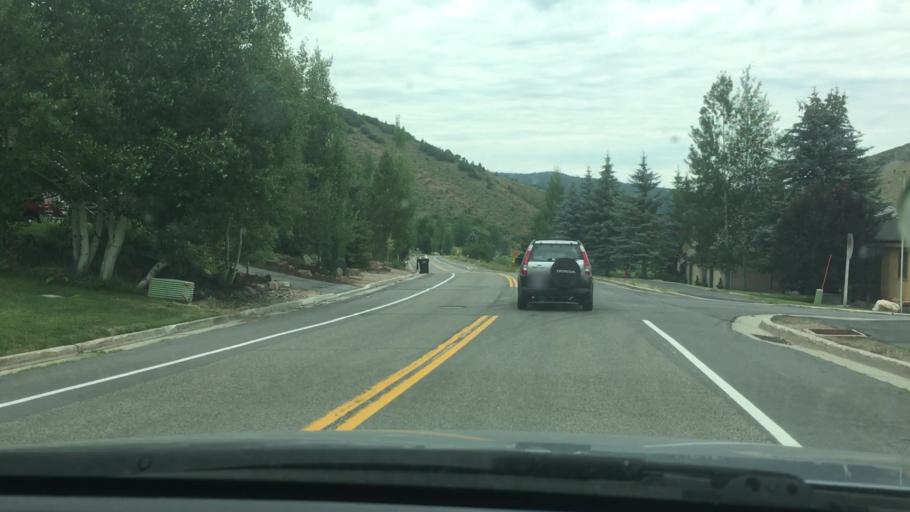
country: US
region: Utah
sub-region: Summit County
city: Summit Park
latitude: 40.7629
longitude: -111.5794
